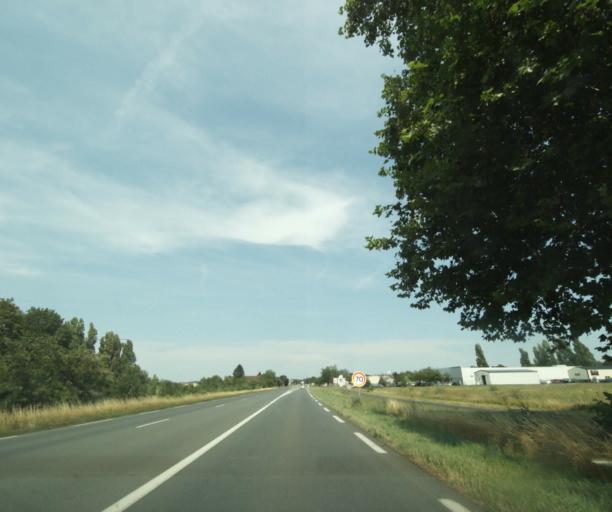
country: FR
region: Poitou-Charentes
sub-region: Departement de la Vienne
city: Dange-Saint-Romain
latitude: 46.9235
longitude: 0.5985
